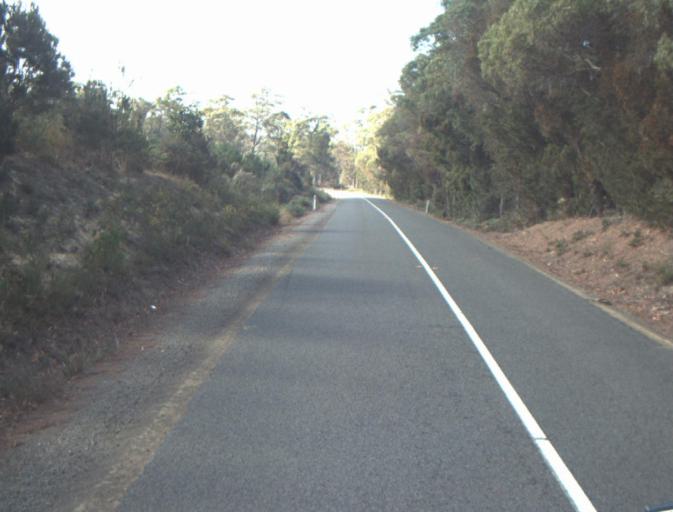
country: AU
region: Tasmania
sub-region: Dorset
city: Bridport
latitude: -41.1437
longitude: 147.2293
